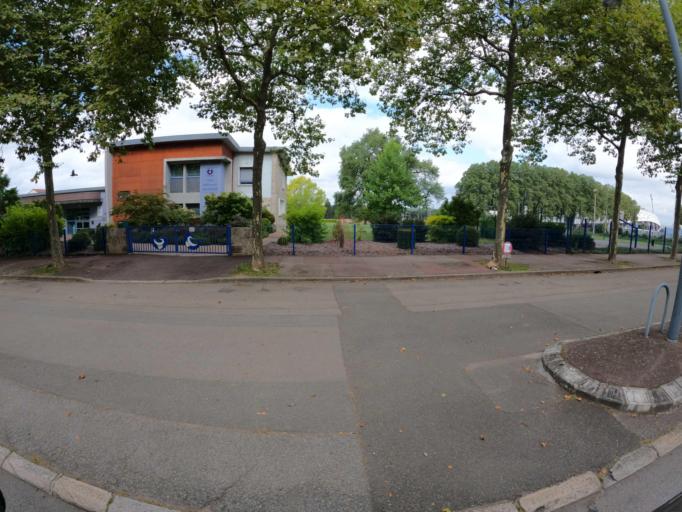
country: FR
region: Limousin
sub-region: Departement de la Haute-Vienne
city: Limoges
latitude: 45.8451
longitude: 1.2414
